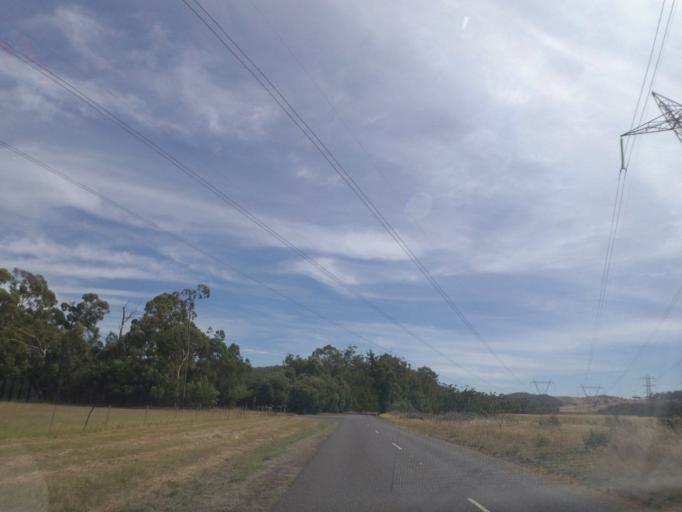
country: AU
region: Victoria
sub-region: Murrindindi
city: Kinglake West
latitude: -37.4613
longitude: 145.3998
